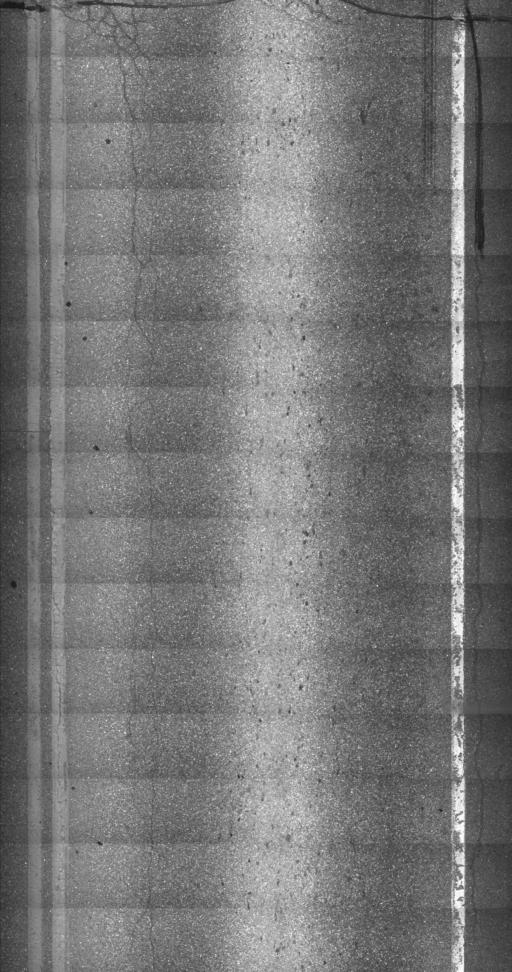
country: US
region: Vermont
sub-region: Chittenden County
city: Milton
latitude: 44.6329
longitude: -73.1149
